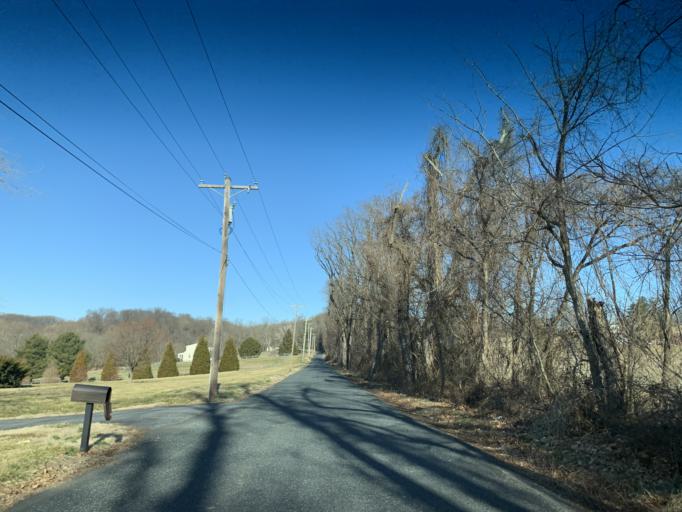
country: US
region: Maryland
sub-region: Harford County
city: South Bel Air
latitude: 39.6180
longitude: -76.2597
